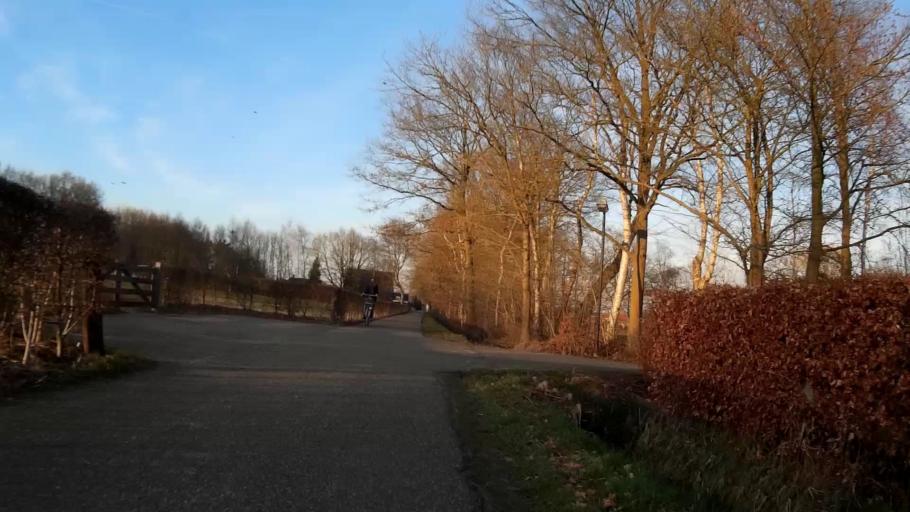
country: NL
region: Utrecht
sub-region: Gemeente Veenendaal
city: Veenendaal
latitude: 52.0195
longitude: 5.5243
